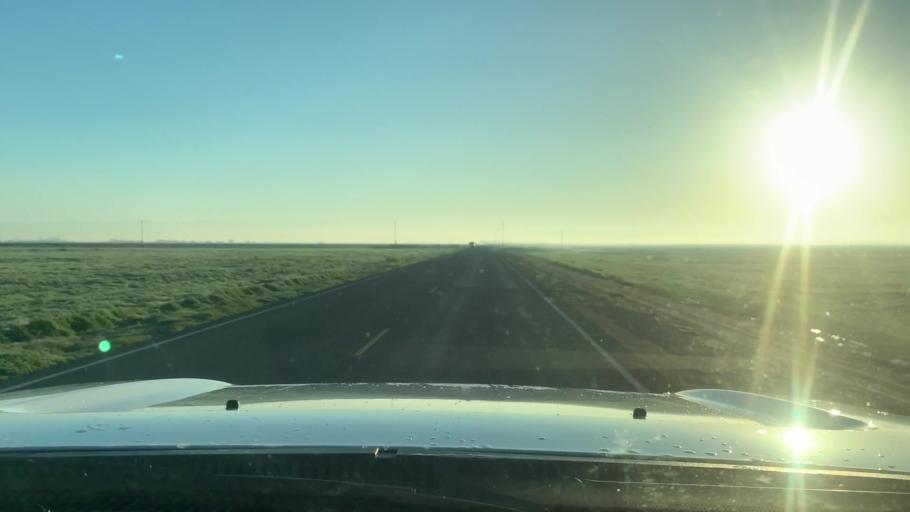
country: US
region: California
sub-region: Kings County
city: Stratford
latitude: 36.2111
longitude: -119.7549
